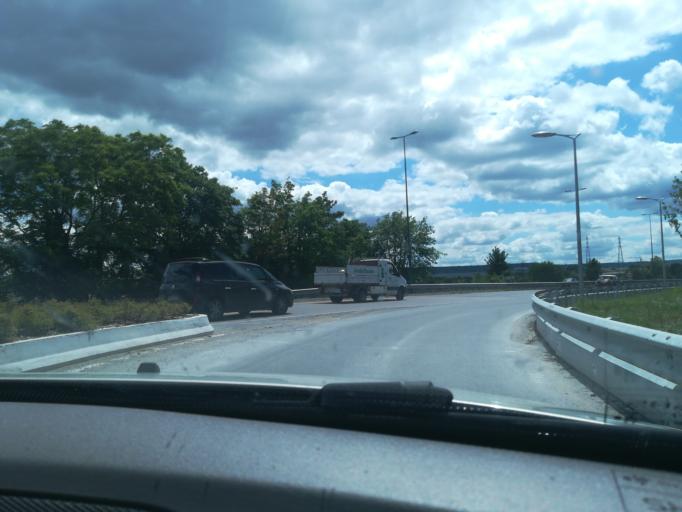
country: FR
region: Champagne-Ardenne
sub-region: Departement de la Marne
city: Bezannes
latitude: 49.2126
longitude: 4.0148
